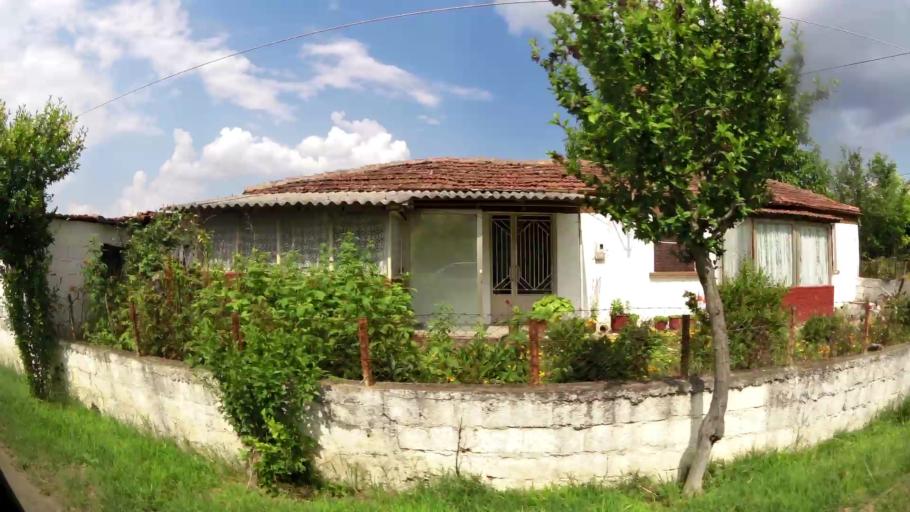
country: GR
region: West Macedonia
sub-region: Nomos Kozanis
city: Koila
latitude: 40.3498
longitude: 21.8386
